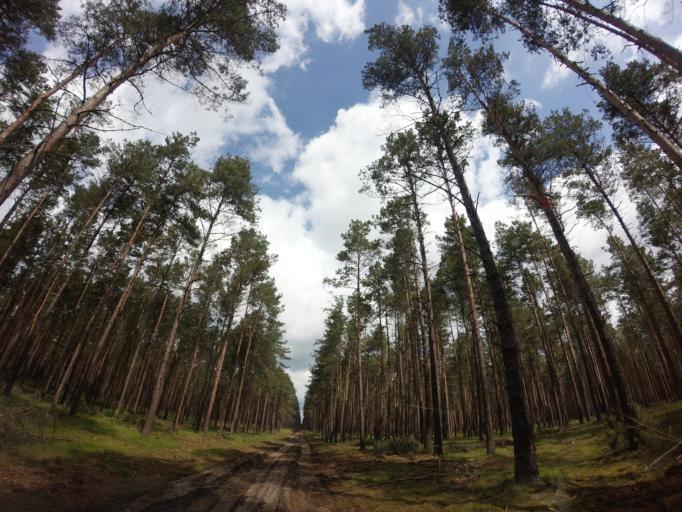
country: PL
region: West Pomeranian Voivodeship
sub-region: Powiat drawski
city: Kalisz Pomorski
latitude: 53.1829
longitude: 15.8997
